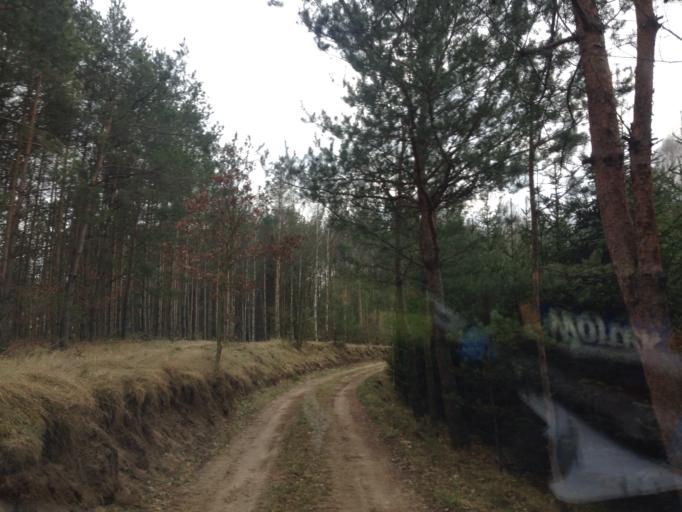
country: PL
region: Warmian-Masurian Voivodeship
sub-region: Powiat dzialdowski
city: Lidzbark
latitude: 53.3742
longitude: 19.7637
